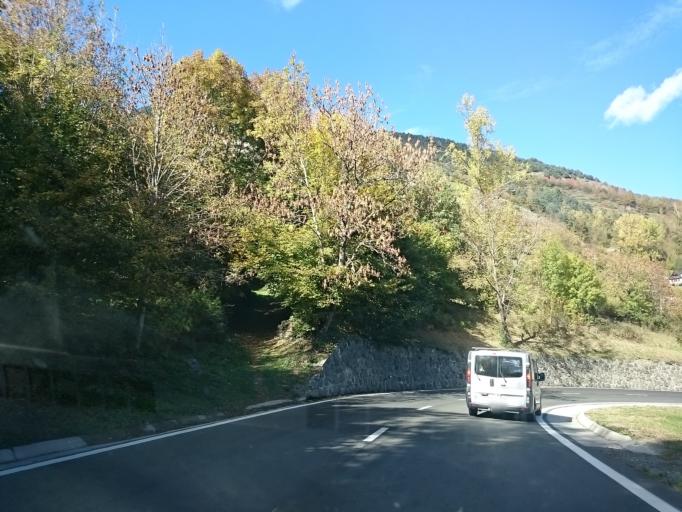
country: ES
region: Catalonia
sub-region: Provincia de Lleida
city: Vielha
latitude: 42.7051
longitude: 0.7890
